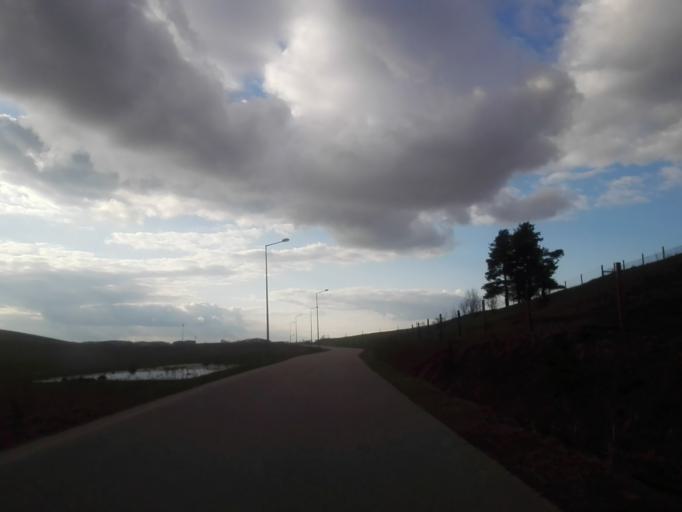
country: PL
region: Podlasie
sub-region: Suwalki
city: Suwalki
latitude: 54.2077
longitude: 22.9775
